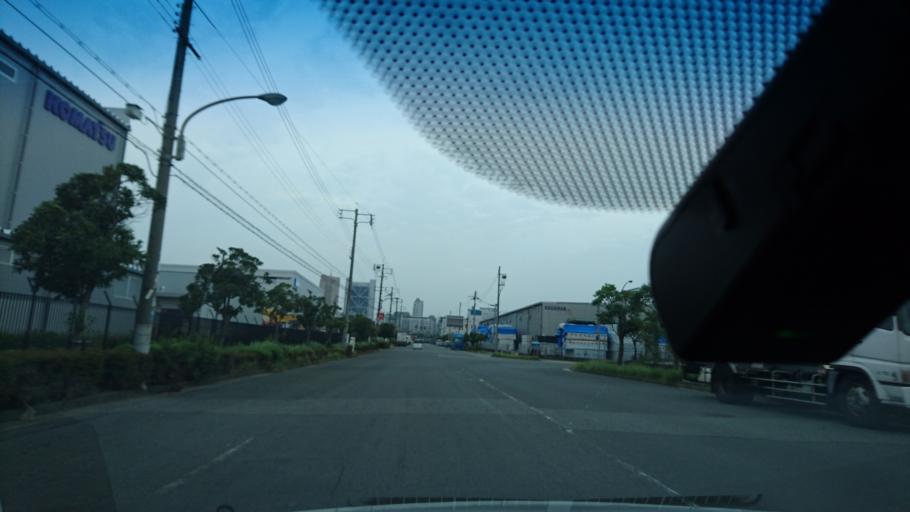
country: JP
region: Hyogo
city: Ashiya
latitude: 34.6879
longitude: 135.2565
